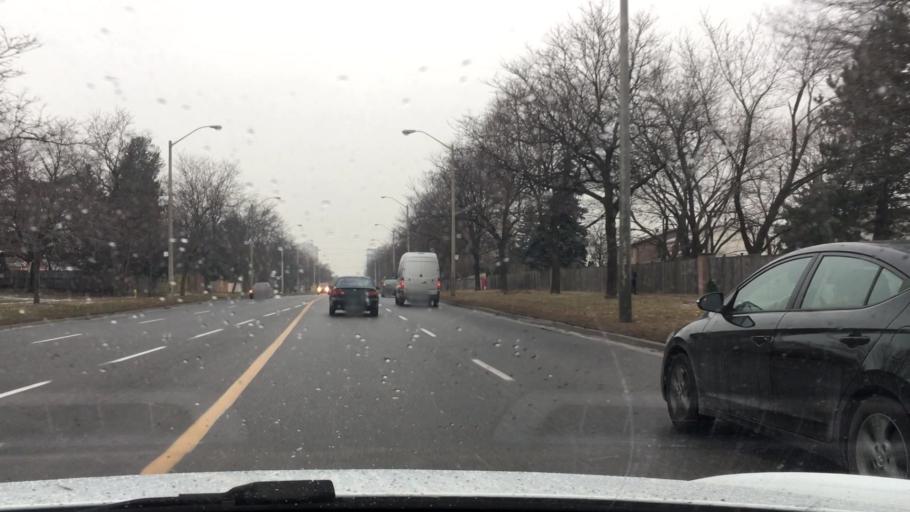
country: CA
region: Ontario
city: Scarborough
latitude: 43.8121
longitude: -79.2694
